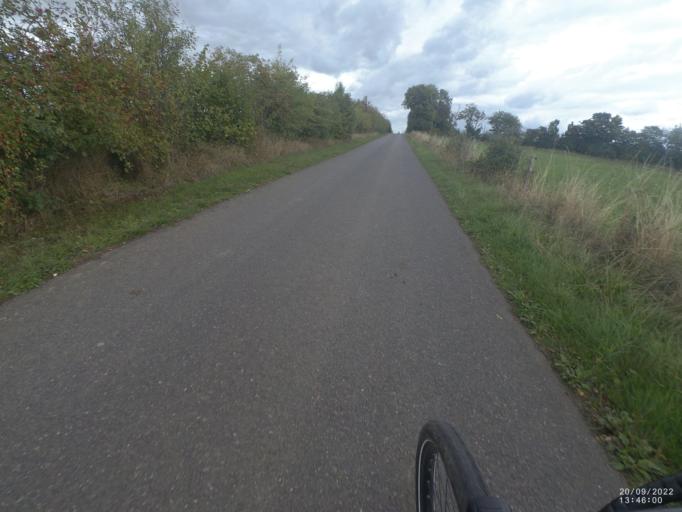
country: DE
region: Rheinland-Pfalz
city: Strohn
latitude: 50.1156
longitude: 6.9291
